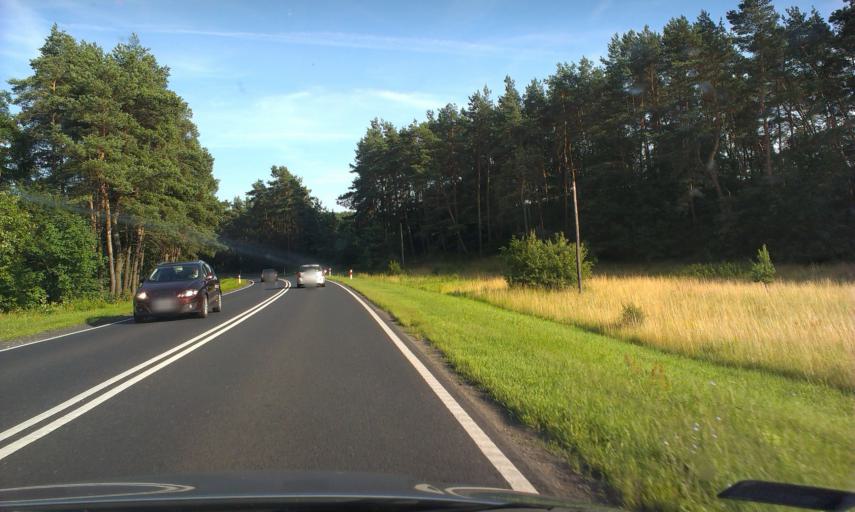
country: PL
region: Kujawsko-Pomorskie
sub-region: Powiat bydgoski
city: Sicienko
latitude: 53.1618
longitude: 17.7916
